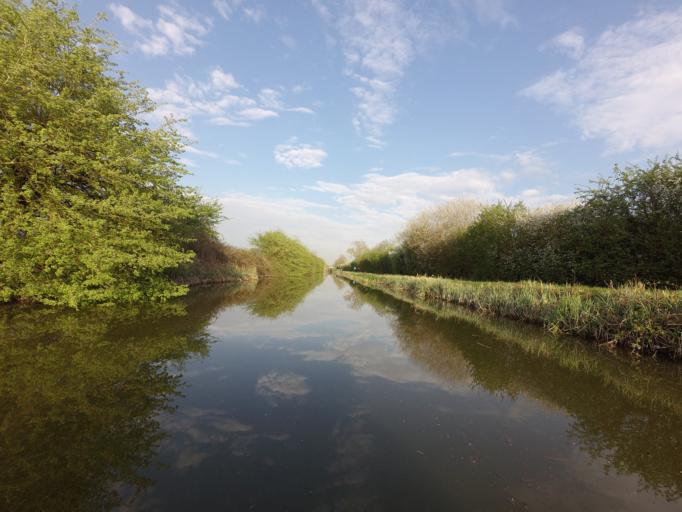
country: GB
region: England
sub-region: Buckinghamshire
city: Aston Clinton
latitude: 51.8173
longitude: -0.7317
